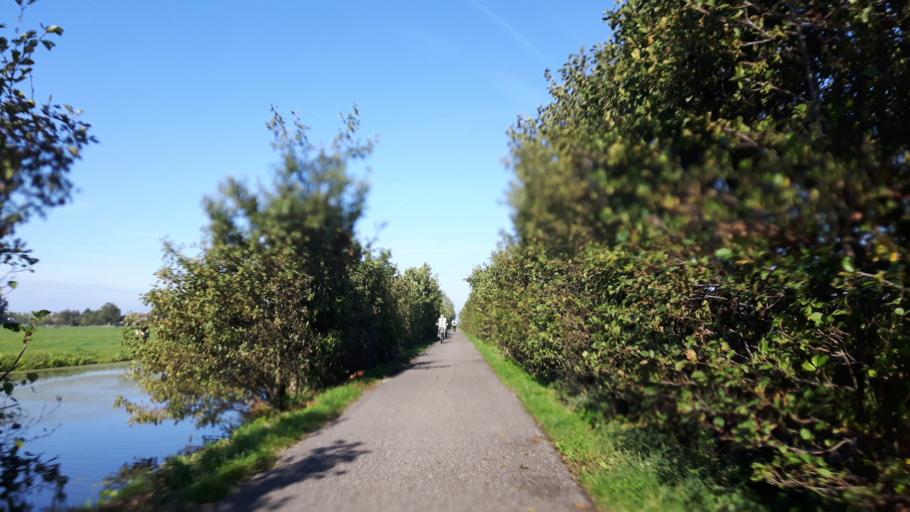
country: NL
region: South Holland
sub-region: Gemeente Vlist
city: Vlist
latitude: 51.9597
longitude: 4.8080
